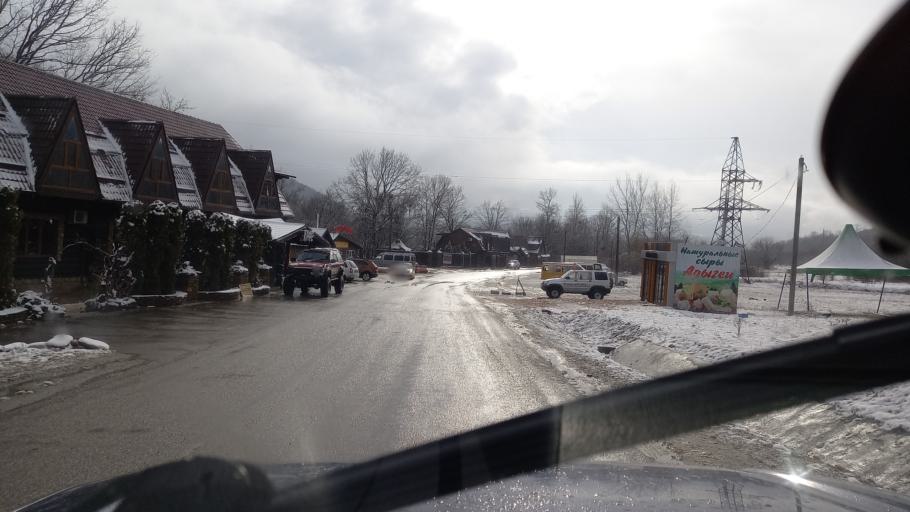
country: RU
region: Adygeya
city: Kamennomostskiy
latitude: 44.2482
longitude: 40.1982
